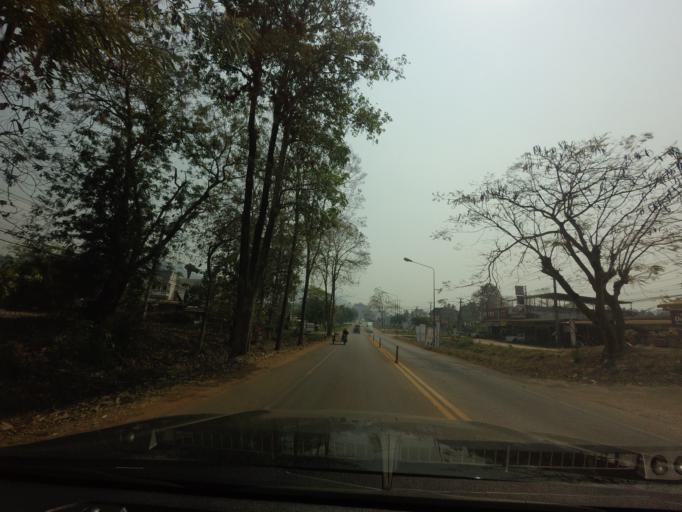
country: TH
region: Kanchanaburi
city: Thong Pha Phum
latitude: 14.7387
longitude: 98.6320
